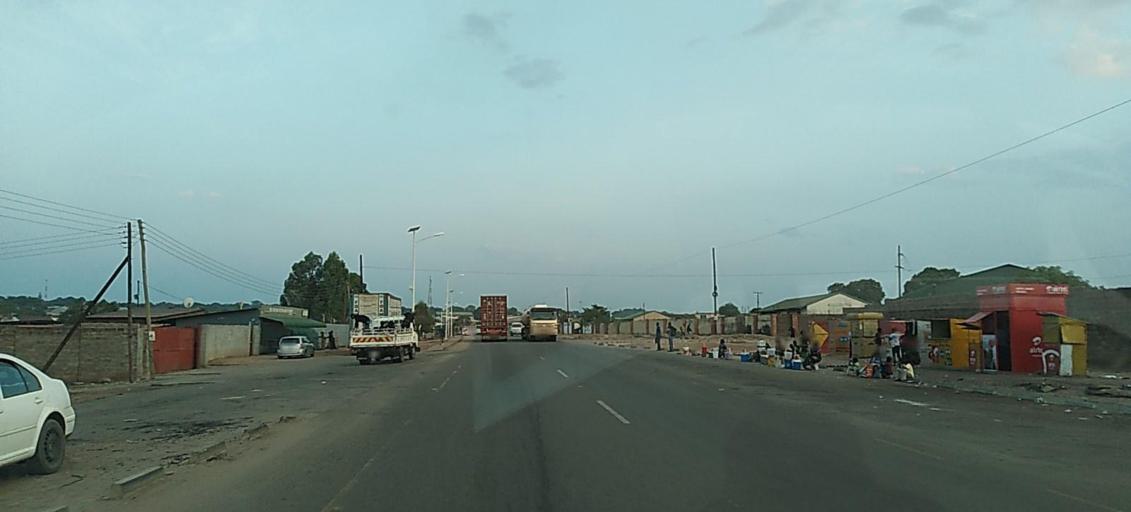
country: ZM
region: Copperbelt
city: Chingola
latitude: -12.5423
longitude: 27.8451
